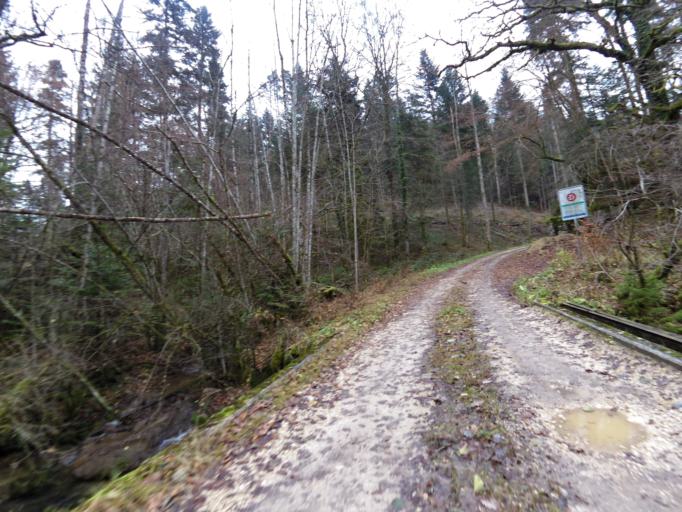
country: FR
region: Alsace
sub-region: Departement du Haut-Rhin
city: Ferrette
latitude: 47.4321
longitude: 7.2777
